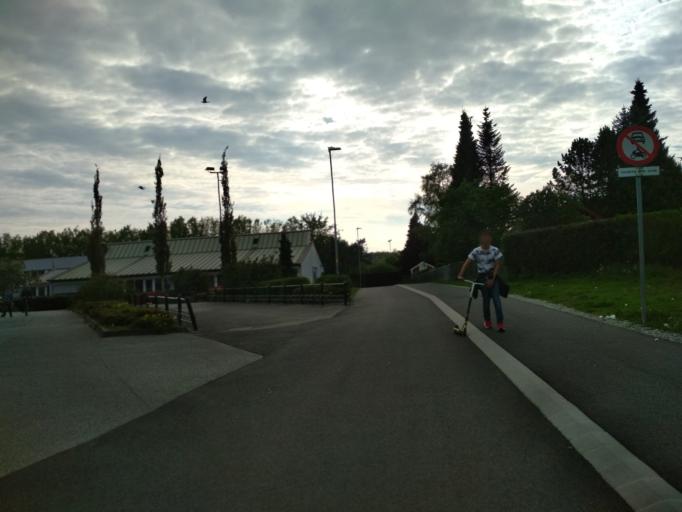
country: NO
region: Rogaland
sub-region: Stavanger
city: Stavanger
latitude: 58.9504
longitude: 5.7240
